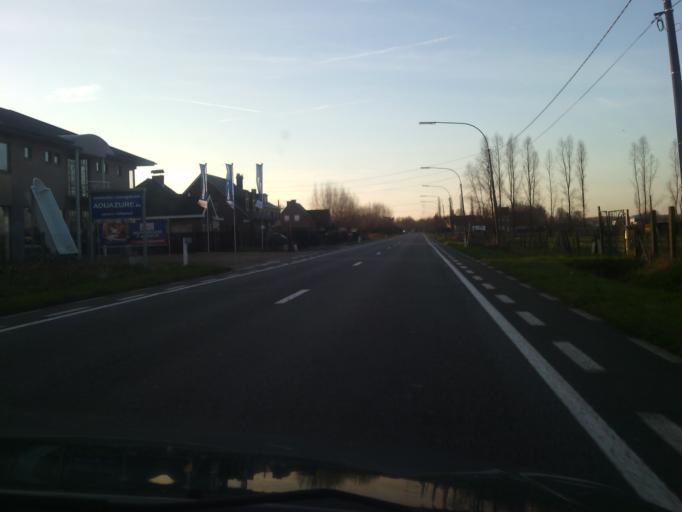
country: BE
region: Flanders
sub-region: Provincie Oost-Vlaanderen
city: Wichelen
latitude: 50.9882
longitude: 3.9738
